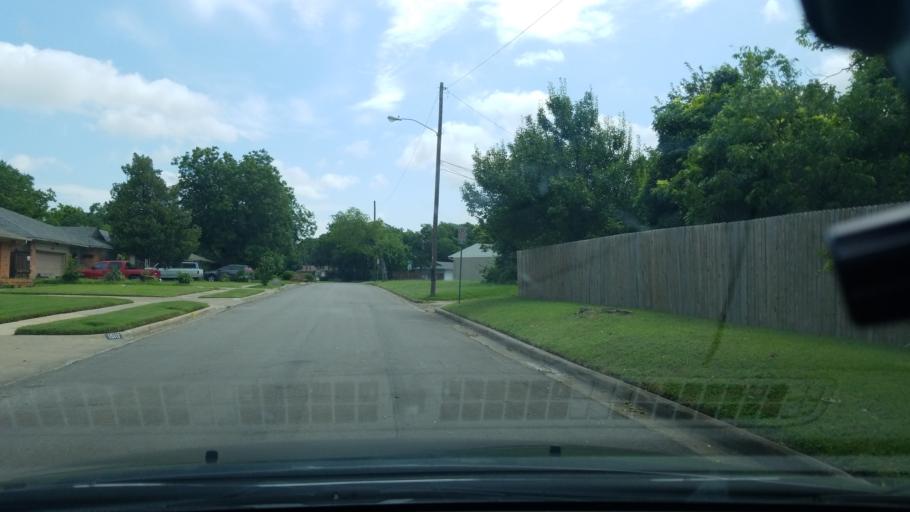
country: US
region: Texas
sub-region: Dallas County
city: Garland
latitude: 32.8292
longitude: -96.6810
